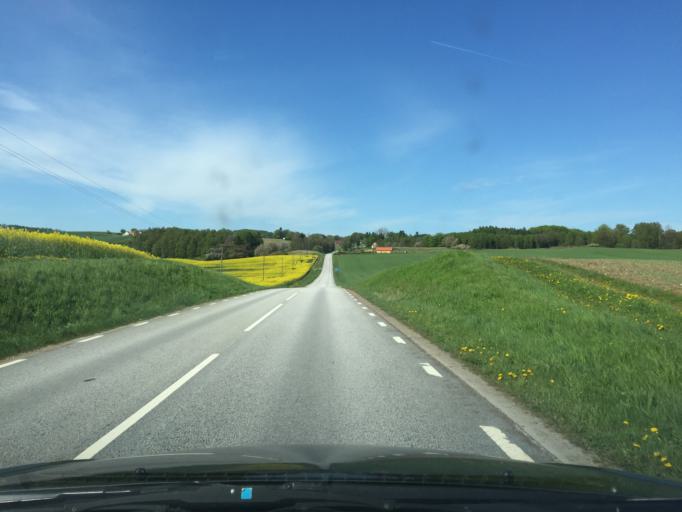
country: SE
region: Skane
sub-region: Skurups Kommun
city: Skurup
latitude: 55.5447
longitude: 13.5150
